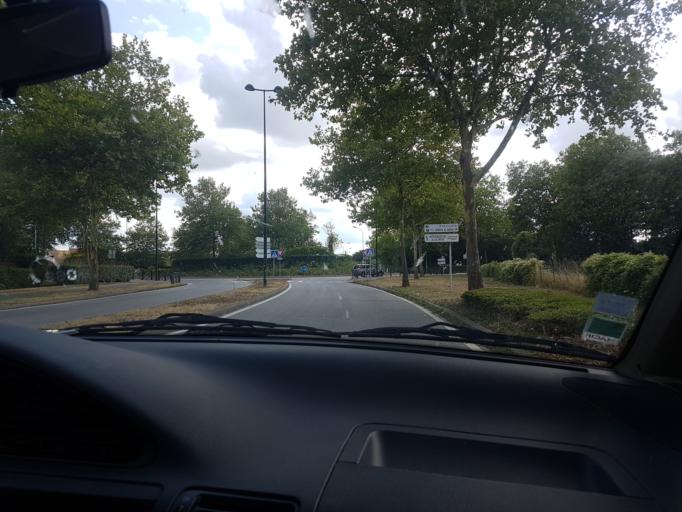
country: FR
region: Ile-de-France
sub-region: Departement des Yvelines
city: Elancourt
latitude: 48.7940
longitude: 1.9623
